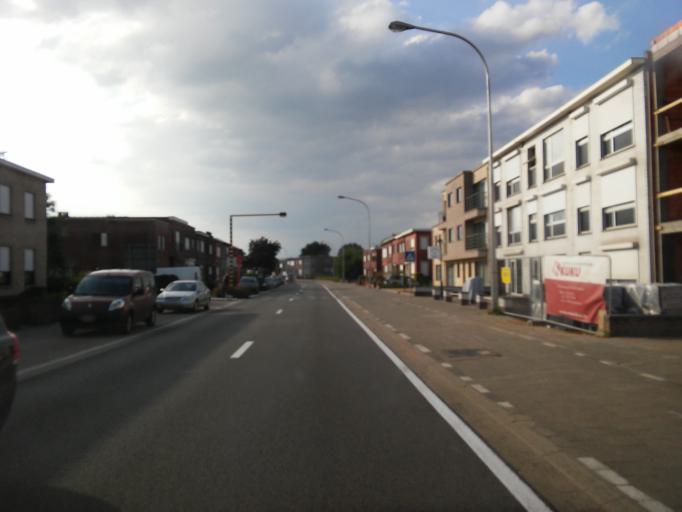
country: BE
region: Flanders
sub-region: Provincie Antwerpen
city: Duffel
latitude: 51.1013
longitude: 4.5044
